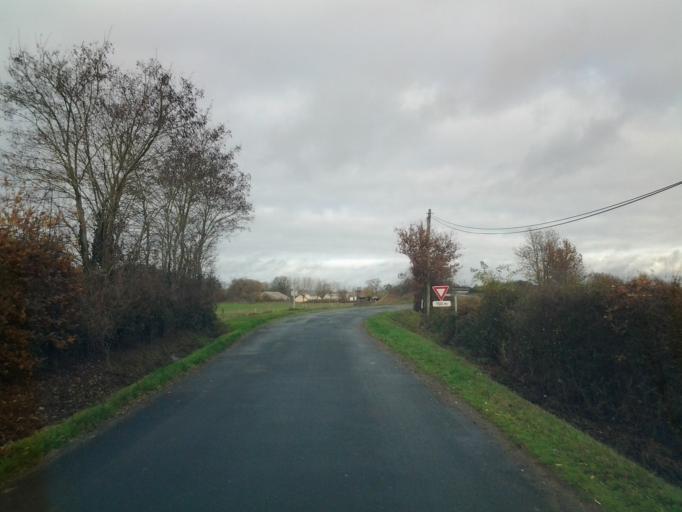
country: FR
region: Pays de la Loire
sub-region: Departement de la Vendee
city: Bournezeau
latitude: 46.6375
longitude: -1.1891
